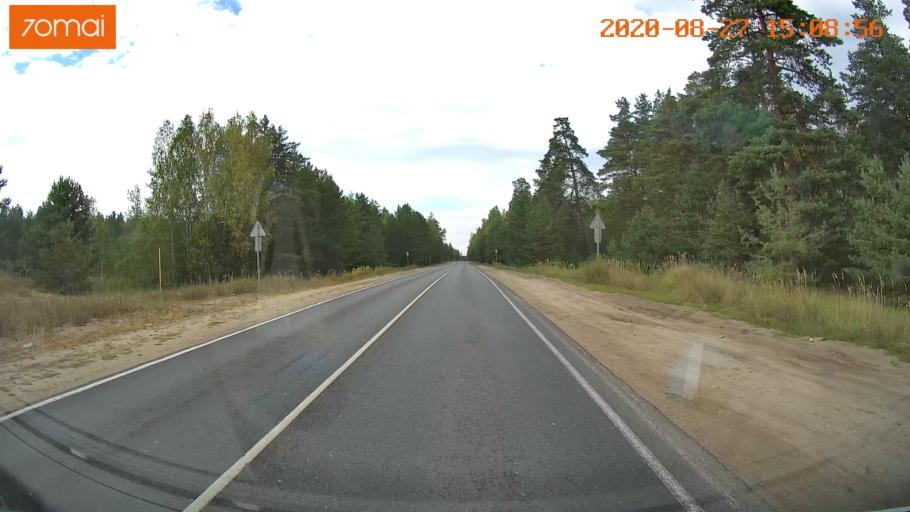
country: RU
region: Vladimir
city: Kurlovo
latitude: 55.4991
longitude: 40.5736
